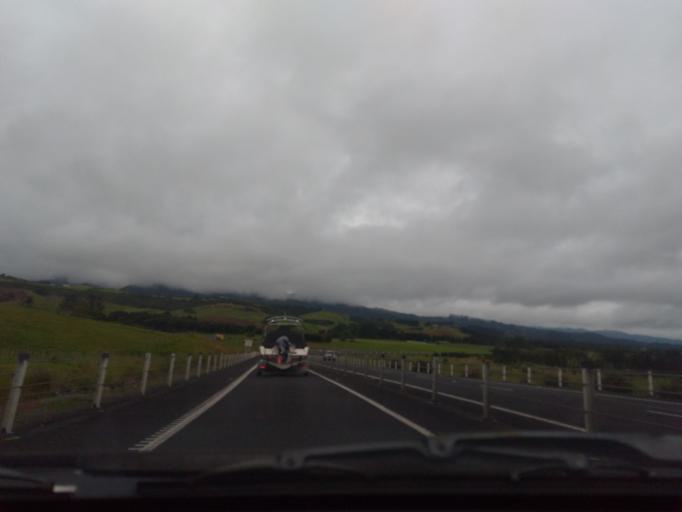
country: NZ
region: Northland
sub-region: Whangarei
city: Ruakaka
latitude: -36.0375
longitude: 174.4179
